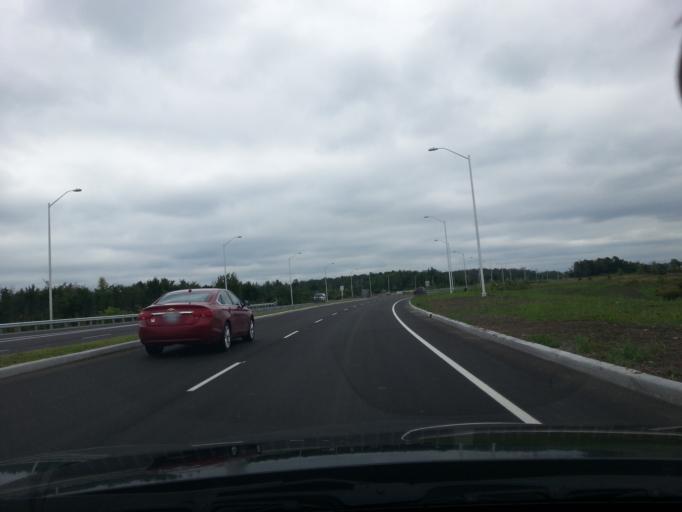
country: CA
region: Ontario
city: Ottawa
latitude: 45.3812
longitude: -75.5860
